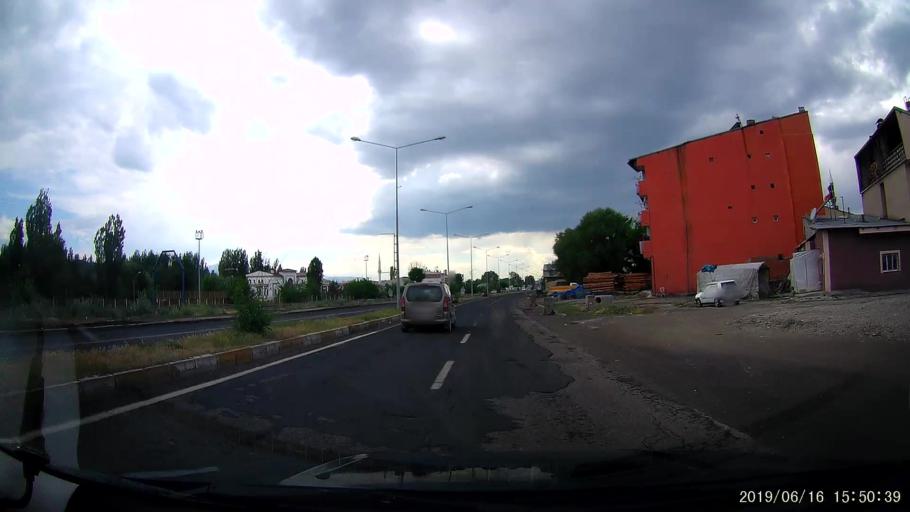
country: TR
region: Erzurum
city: Pasinler
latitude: 39.9771
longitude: 41.6800
